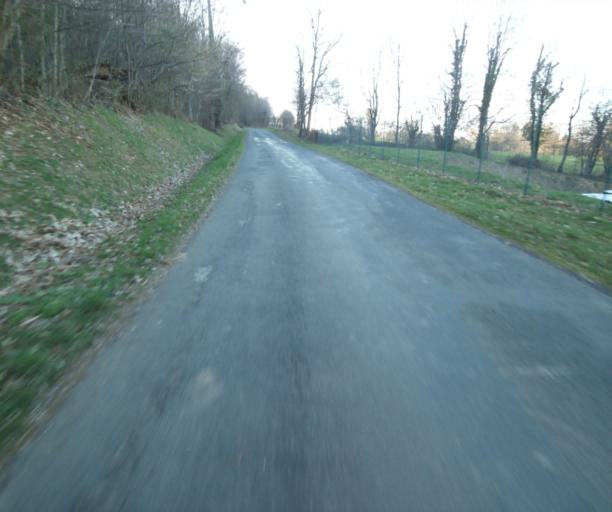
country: FR
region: Limousin
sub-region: Departement de la Correze
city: Seilhac
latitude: 45.3591
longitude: 1.7093
